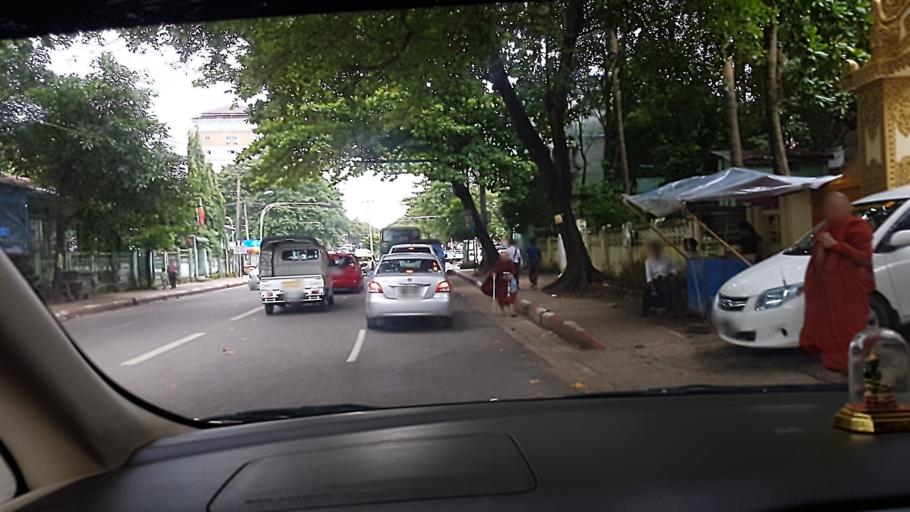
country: MM
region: Yangon
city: Yangon
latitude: 16.8038
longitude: 96.1291
